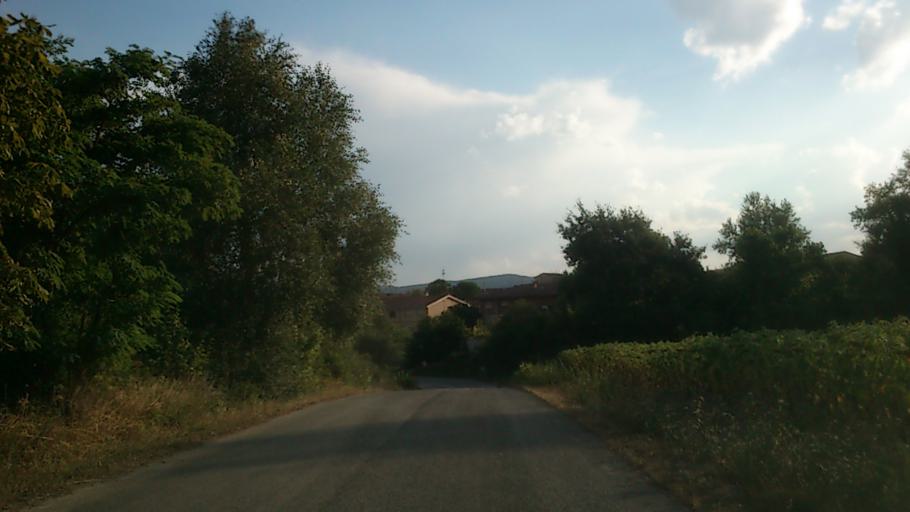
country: ES
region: Castille and Leon
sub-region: Provincia de Burgos
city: Frias
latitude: 42.7958
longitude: -3.2679
